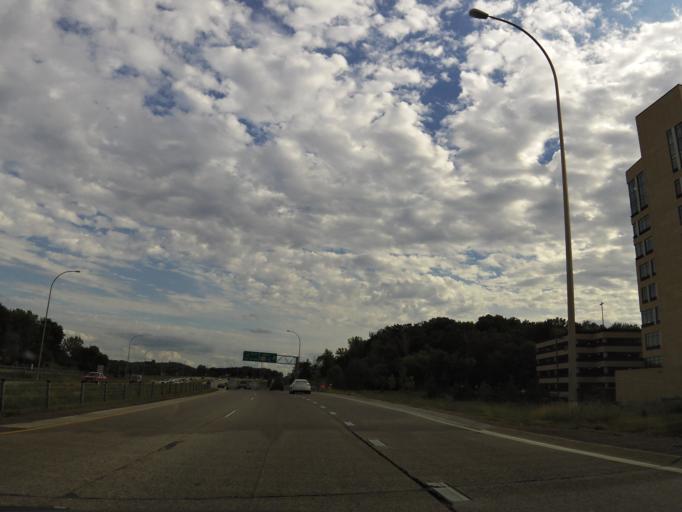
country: US
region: Minnesota
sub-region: Hennepin County
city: Edina
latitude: 44.8957
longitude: -93.4012
